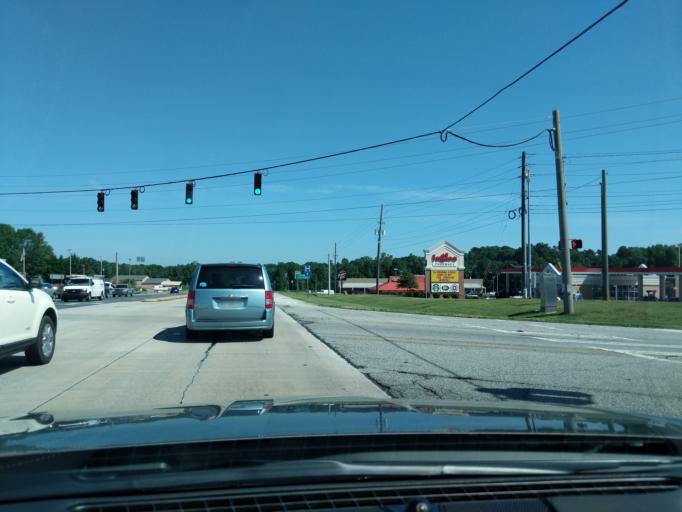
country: US
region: Georgia
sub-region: Habersham County
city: Cornelia
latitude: 34.5106
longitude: -83.5450
